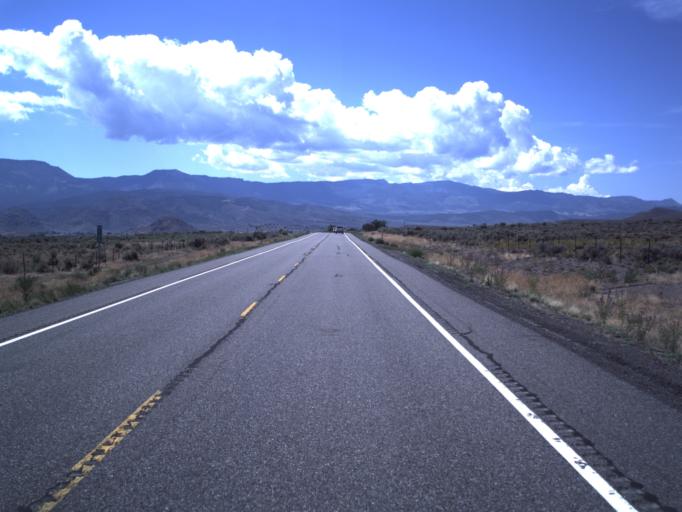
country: US
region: Utah
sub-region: Piute County
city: Junction
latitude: 38.2623
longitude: -112.2212
